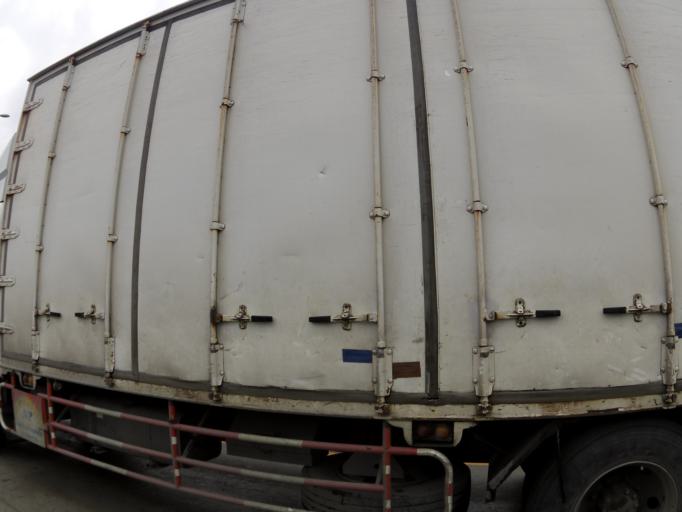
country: TH
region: Chon Buri
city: Bang Lamung
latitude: 13.1026
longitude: 100.9096
